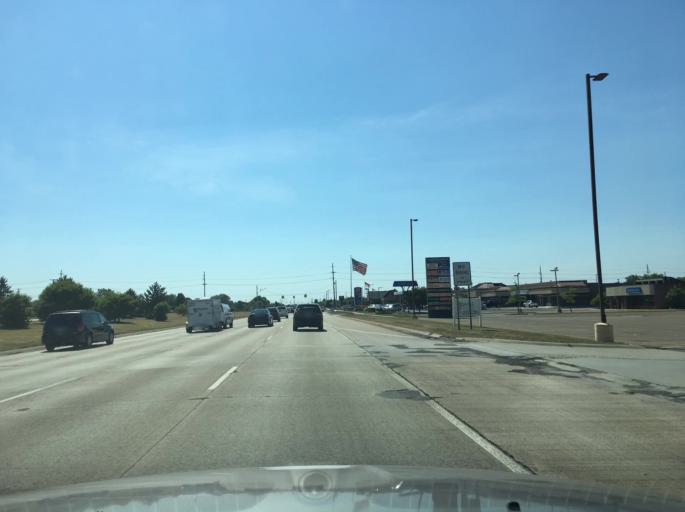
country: US
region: Michigan
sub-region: Macomb County
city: Utica
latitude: 42.6279
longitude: -82.9704
